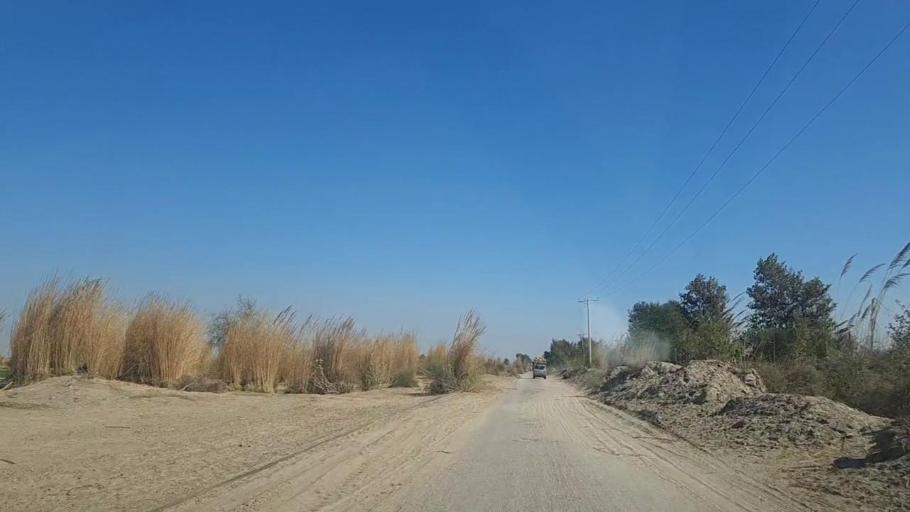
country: PK
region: Sindh
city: Khadro
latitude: 26.2093
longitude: 68.8725
